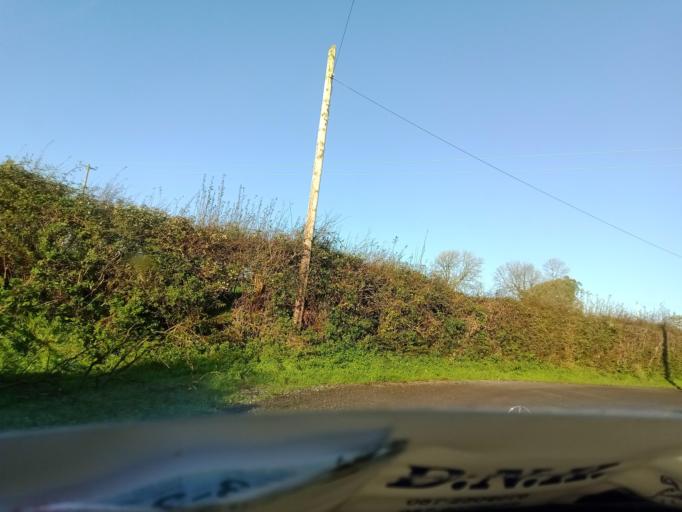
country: IE
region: Leinster
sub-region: Kilkenny
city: Mooncoin
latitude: 52.2914
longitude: -7.1763
